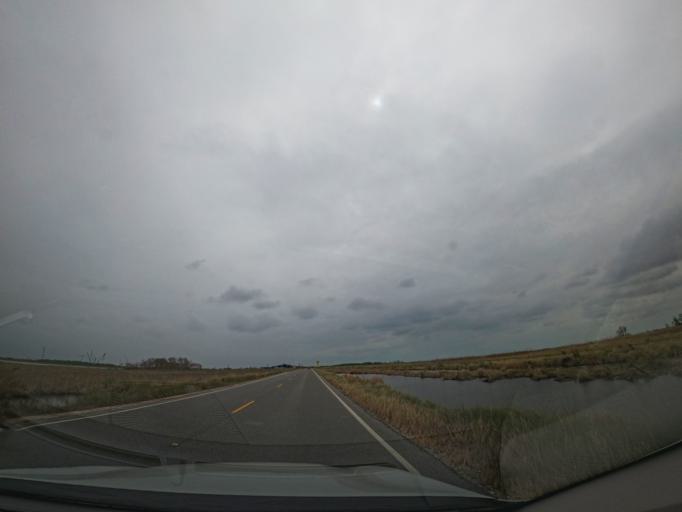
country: US
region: Louisiana
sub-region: Cameron Parish
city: Cameron
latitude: 29.7923
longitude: -93.3495
